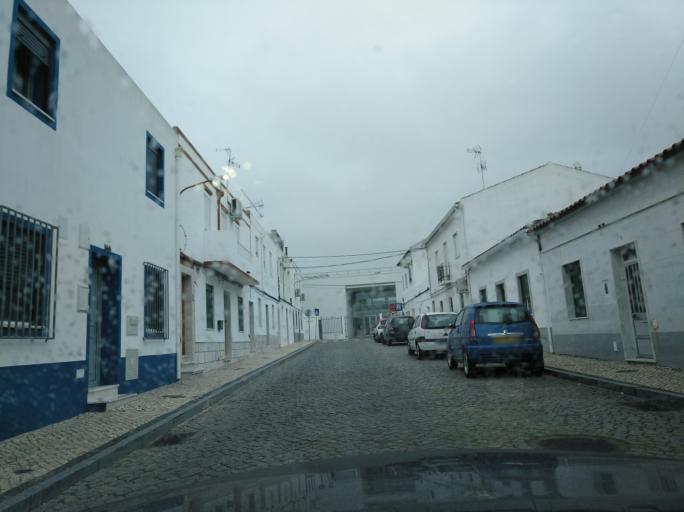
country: PT
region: Portalegre
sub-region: Campo Maior
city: Campo Maior
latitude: 39.0180
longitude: -7.0657
